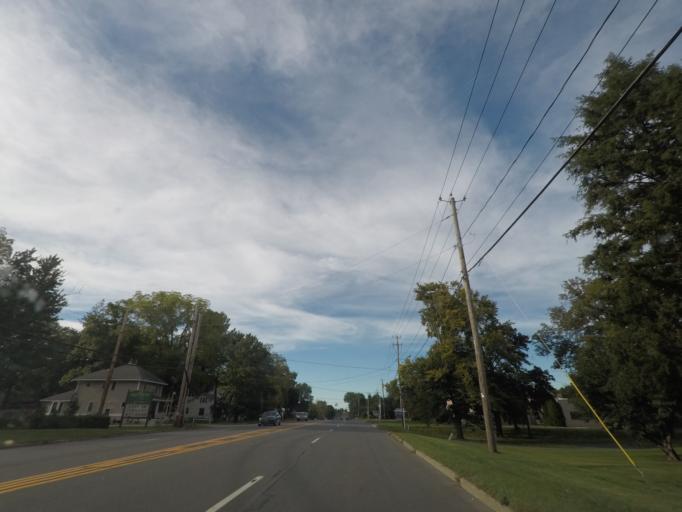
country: US
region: New York
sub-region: Rensselaer County
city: East Greenbush
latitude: 42.5759
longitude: -73.6895
